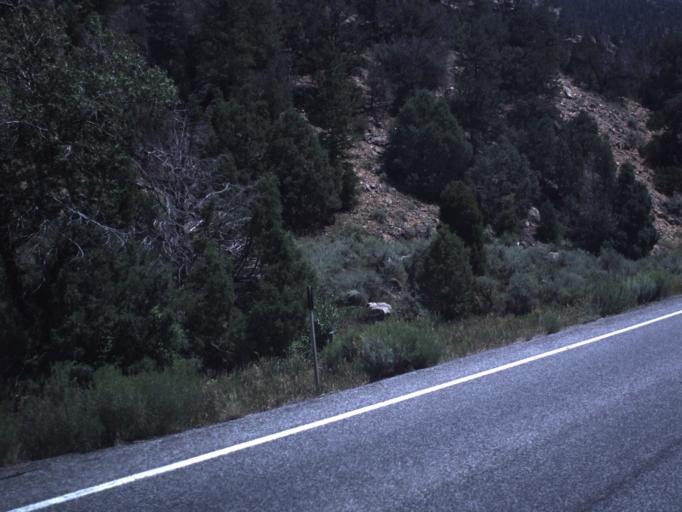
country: US
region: Utah
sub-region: Emery County
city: Huntington
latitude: 39.4398
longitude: -111.1340
